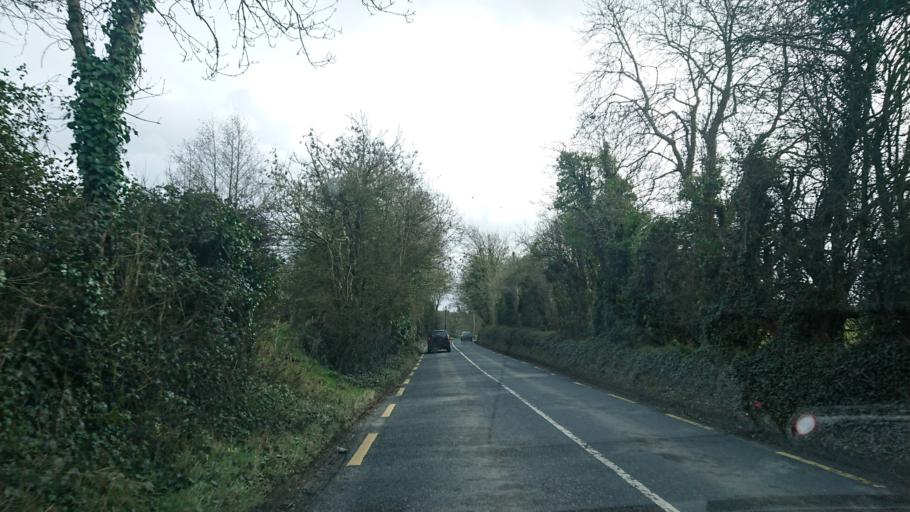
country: IE
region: Leinster
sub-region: Kildare
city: Eadestown
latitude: 53.1927
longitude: -6.5608
